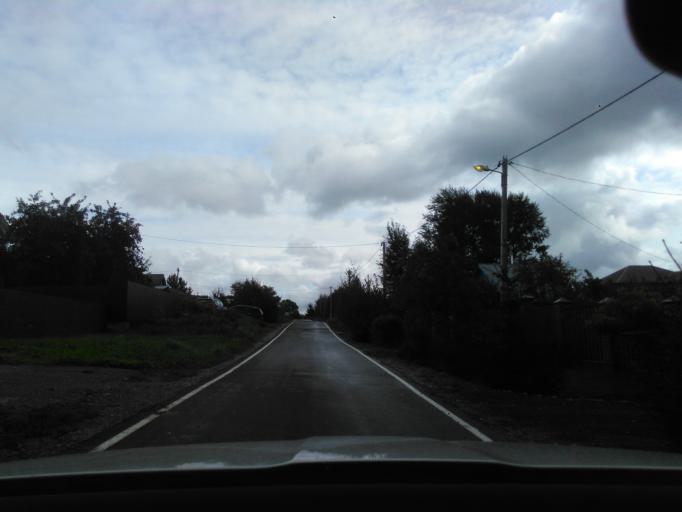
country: RU
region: Moskovskaya
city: Lozhki
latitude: 56.1230
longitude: 37.0989
